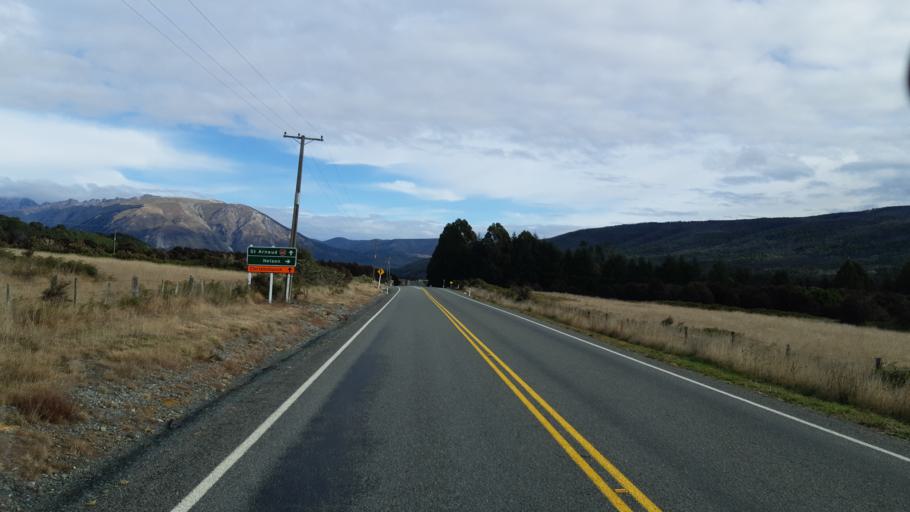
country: NZ
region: Tasman
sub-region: Tasman District
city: Wakefield
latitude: -41.7842
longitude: 172.8970
